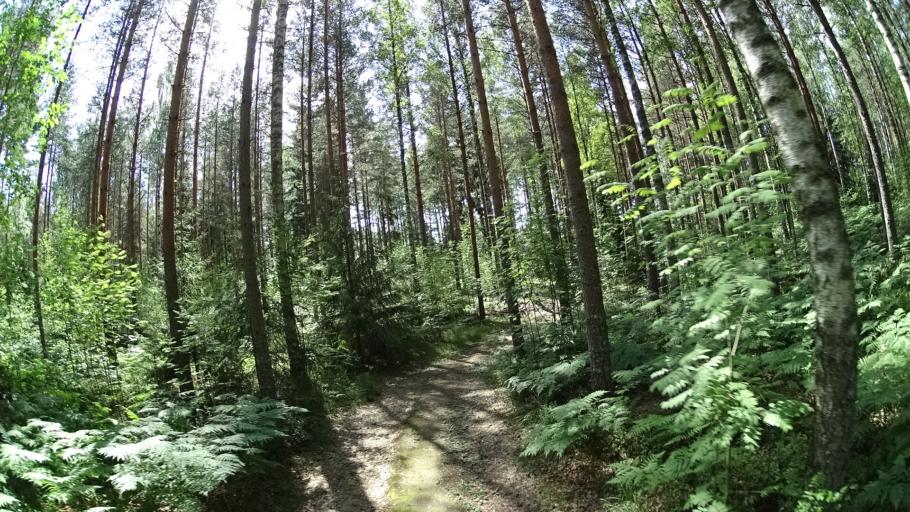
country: FI
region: Haeme
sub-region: Forssa
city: Tammela
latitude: 60.7715
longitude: 23.8677
